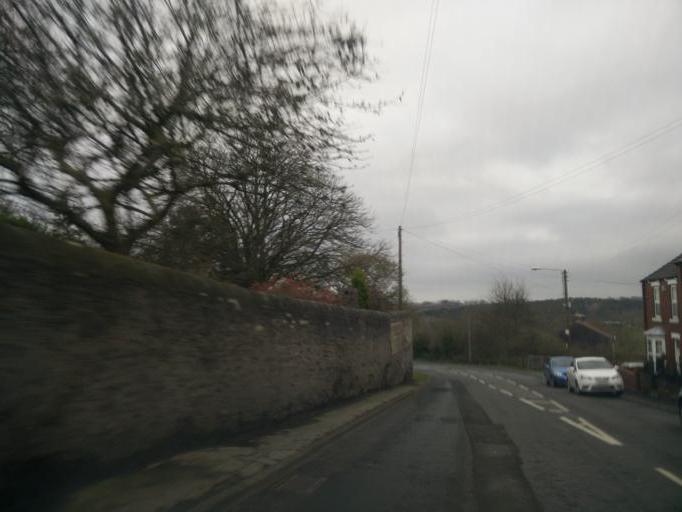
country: GB
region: England
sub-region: County Durham
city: Crook
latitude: 54.7294
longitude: -1.7527
